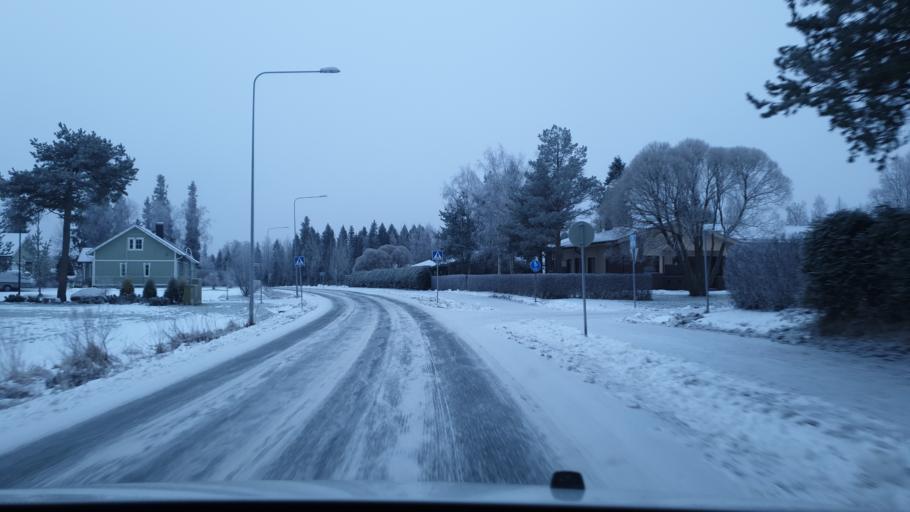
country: FI
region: Lapland
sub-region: Kemi-Tornio
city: Kemi
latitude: 65.7390
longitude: 24.6076
